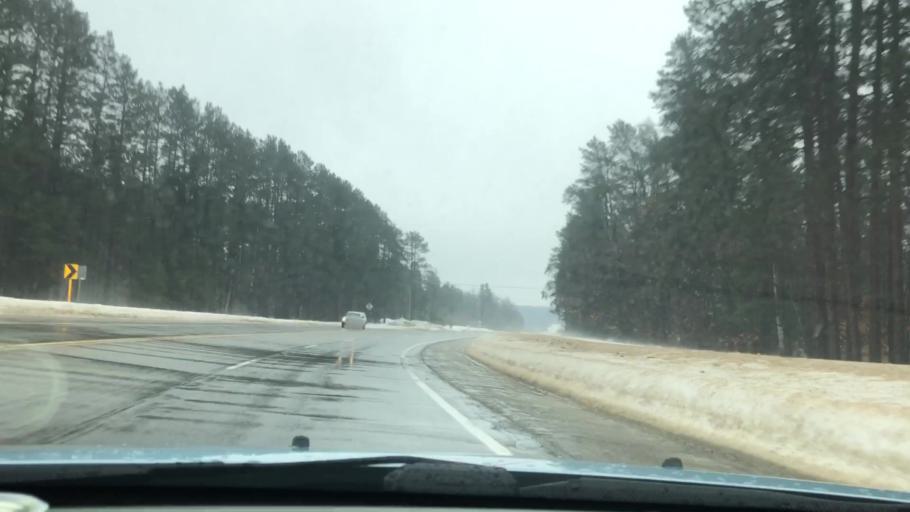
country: US
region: Michigan
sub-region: Otsego County
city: Gaylord
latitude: 45.0591
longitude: -84.7761
